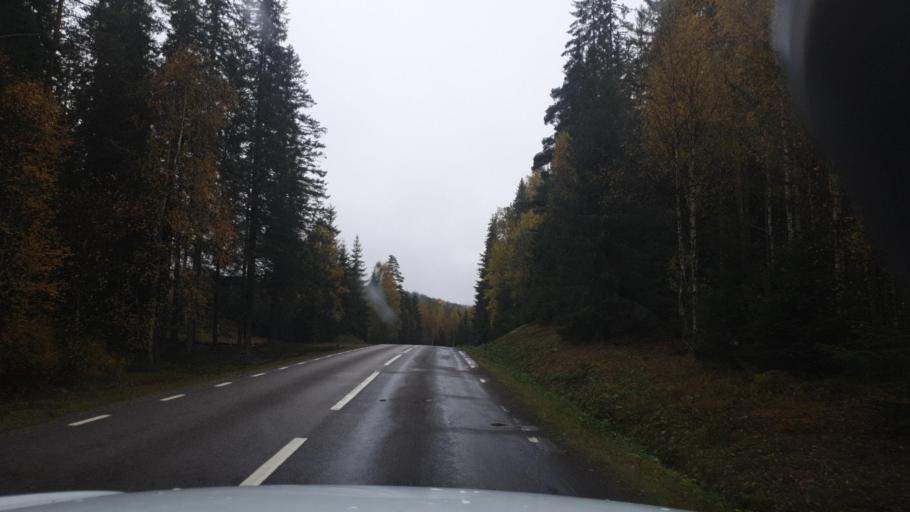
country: SE
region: Vaermland
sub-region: Eda Kommun
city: Amotfors
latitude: 59.6656
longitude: 12.3821
